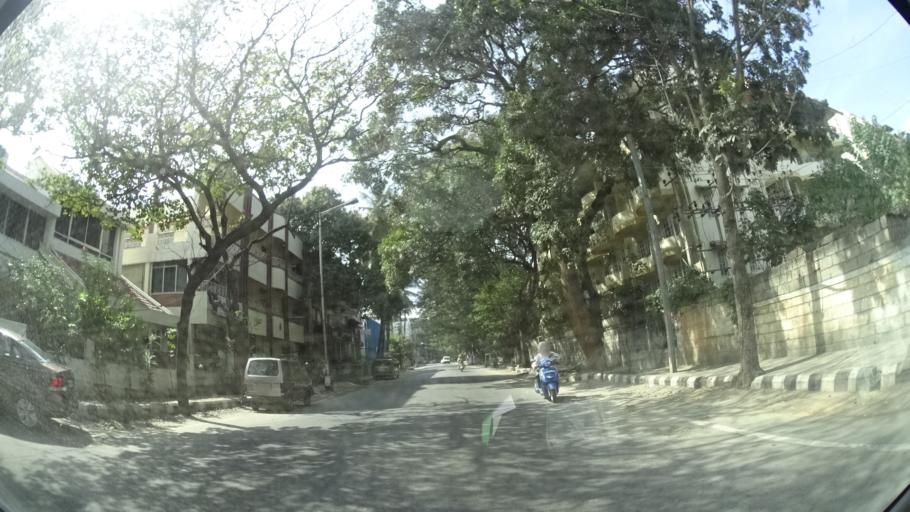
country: IN
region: Karnataka
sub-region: Bangalore Urban
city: Bangalore
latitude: 13.0026
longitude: 77.5977
